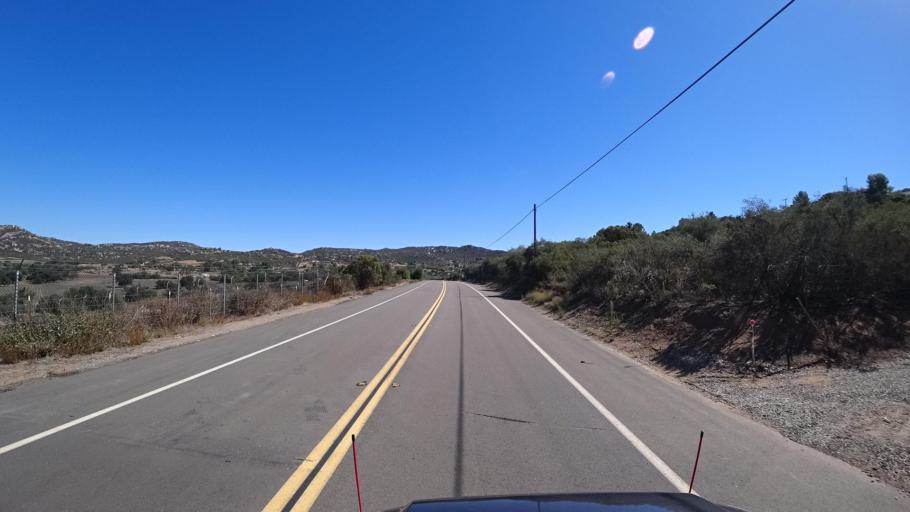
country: US
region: California
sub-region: San Diego County
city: Alpine
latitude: 32.7646
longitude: -116.6876
